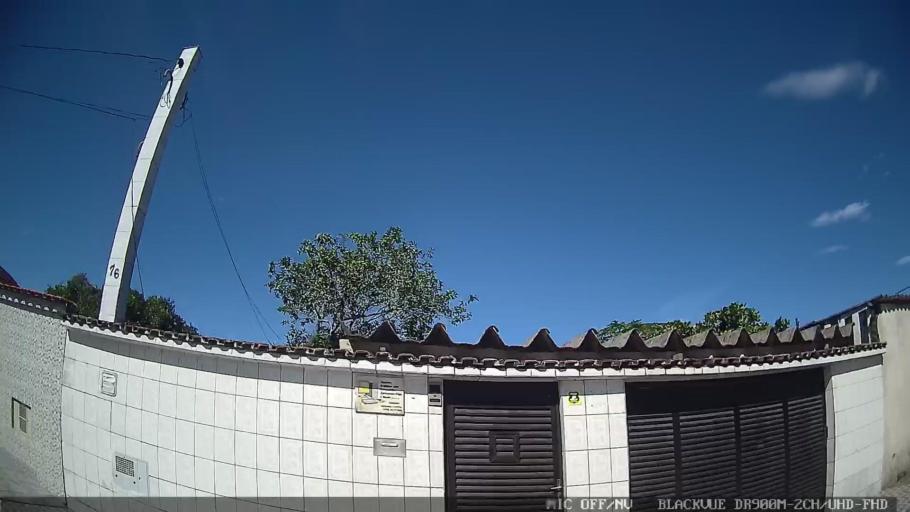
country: BR
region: Sao Paulo
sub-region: Santos
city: Santos
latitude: -23.9390
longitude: -46.2956
